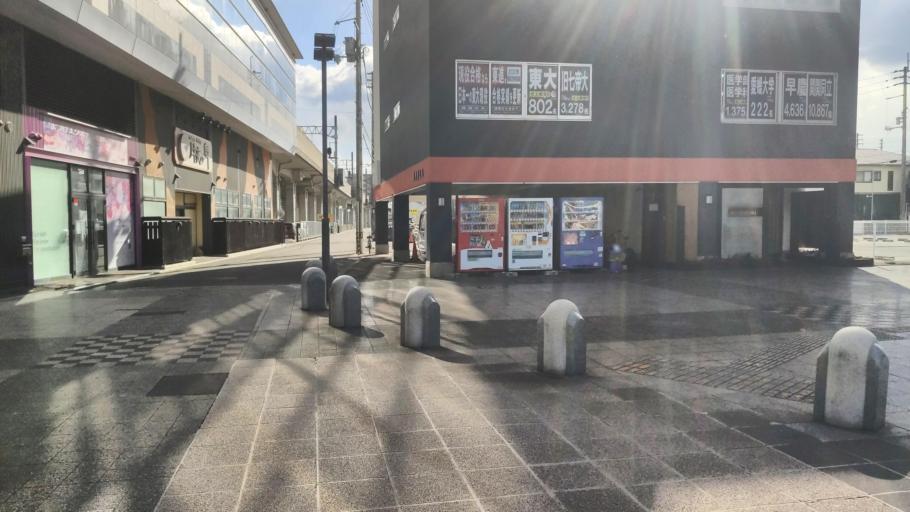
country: JP
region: Ehime
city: Hojo
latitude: 34.0640
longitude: 132.9936
